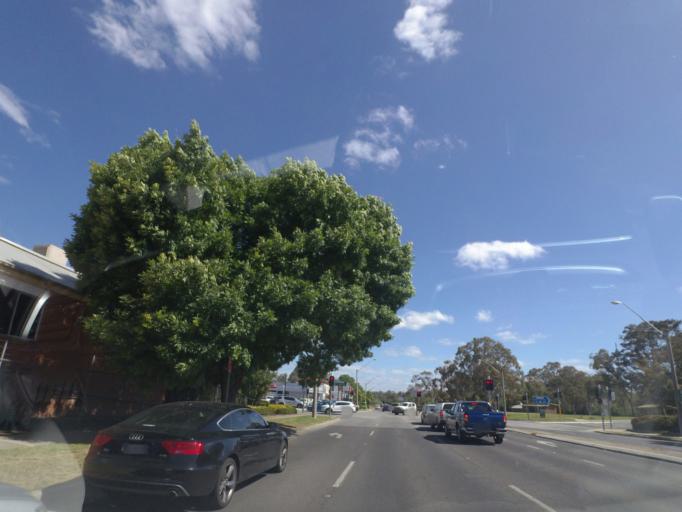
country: AU
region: New South Wales
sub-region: Albury Municipality
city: South Albury
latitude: -36.0836
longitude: 146.9100
